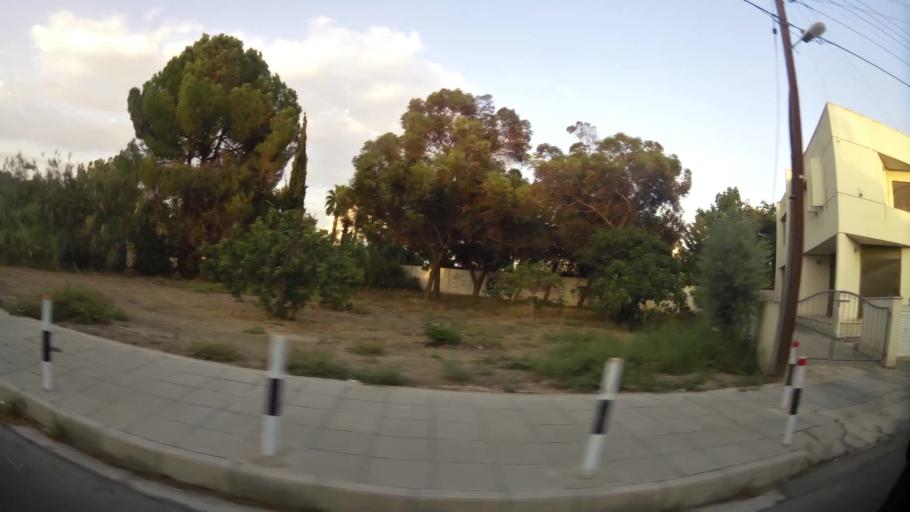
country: CY
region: Lefkosia
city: Nicosia
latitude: 35.1630
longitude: 33.3258
